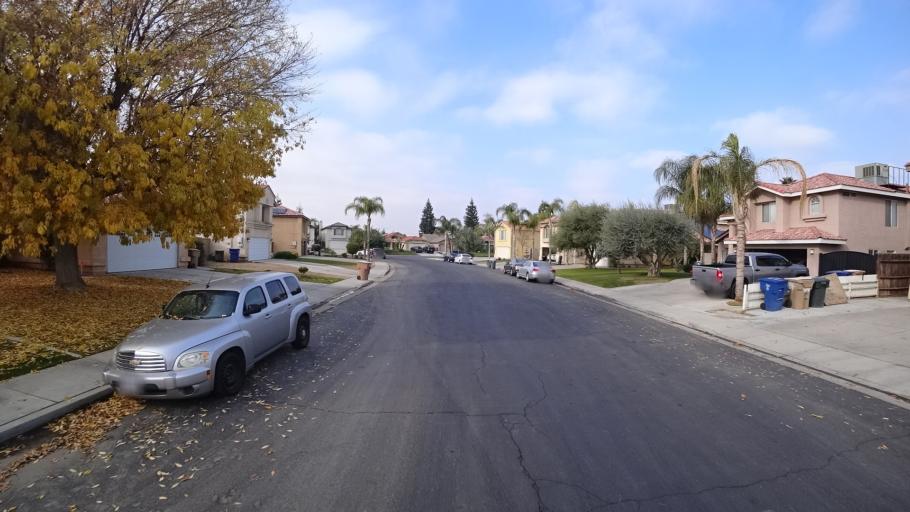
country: US
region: California
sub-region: Kern County
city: Greenfield
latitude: 35.3011
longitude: -119.0714
